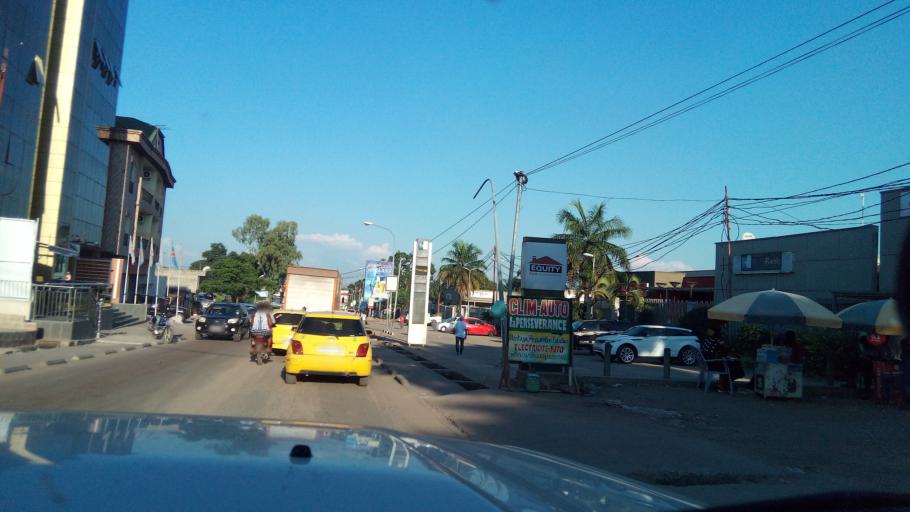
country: CD
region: Kinshasa
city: Kinshasa
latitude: -4.3460
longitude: 15.2662
